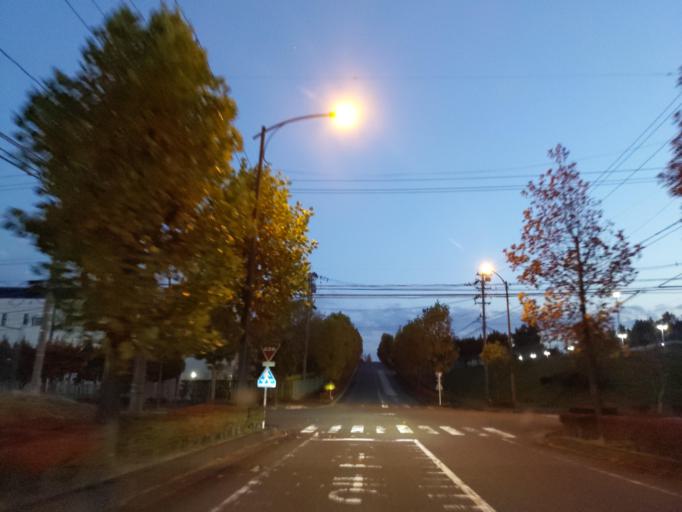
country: JP
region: Fukushima
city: Koriyama
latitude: 37.4429
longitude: 140.3061
